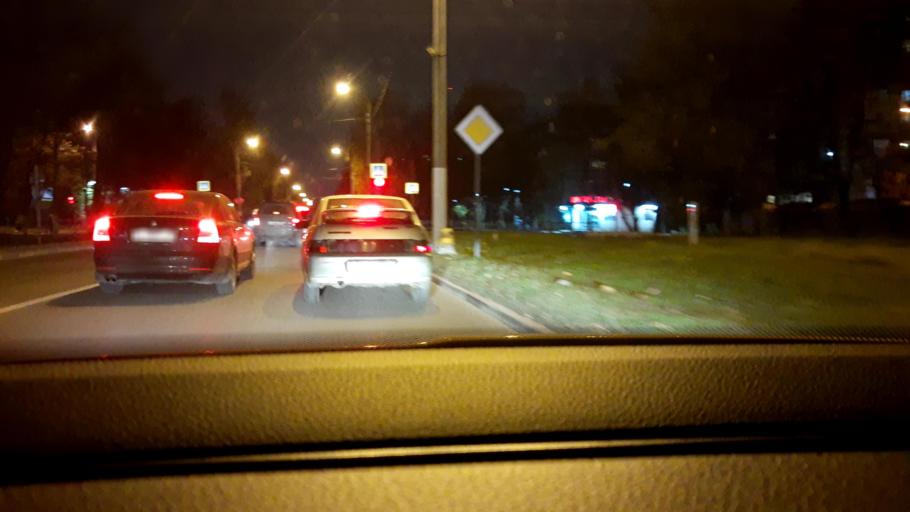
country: RU
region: Moskovskaya
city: Dolgoprudnyy
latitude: 55.9451
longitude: 37.5074
